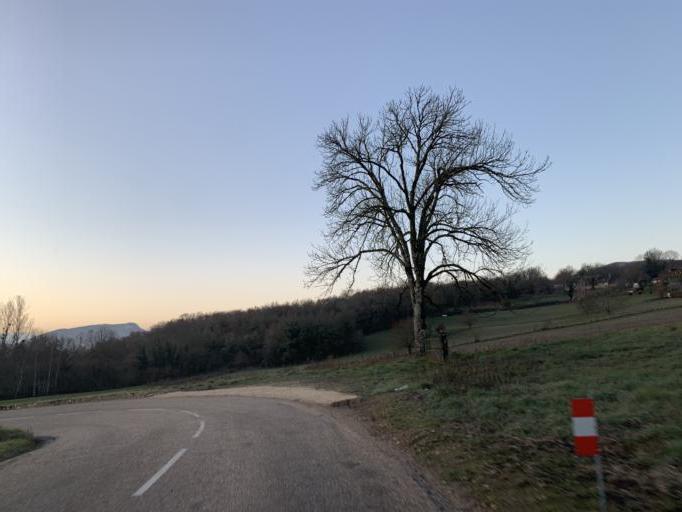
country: FR
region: Rhone-Alpes
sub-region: Departement de l'Ain
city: Belley
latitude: 45.7777
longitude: 5.6590
